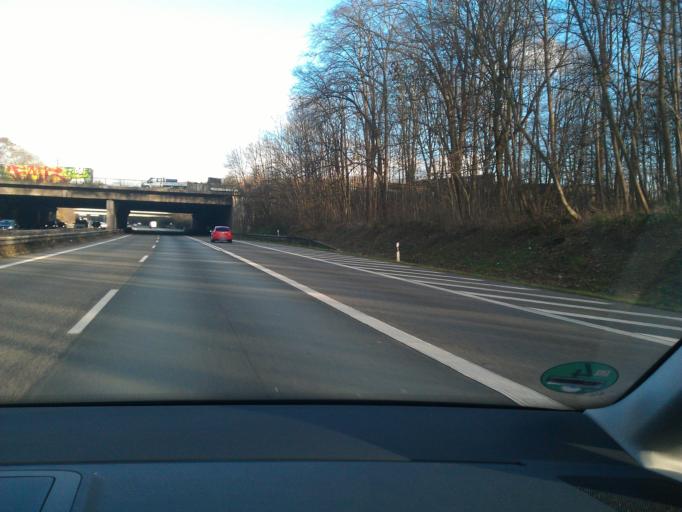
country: DE
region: North Rhine-Westphalia
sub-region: Regierungsbezirk Koln
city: Mengenich
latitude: 50.9991
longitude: 6.8967
